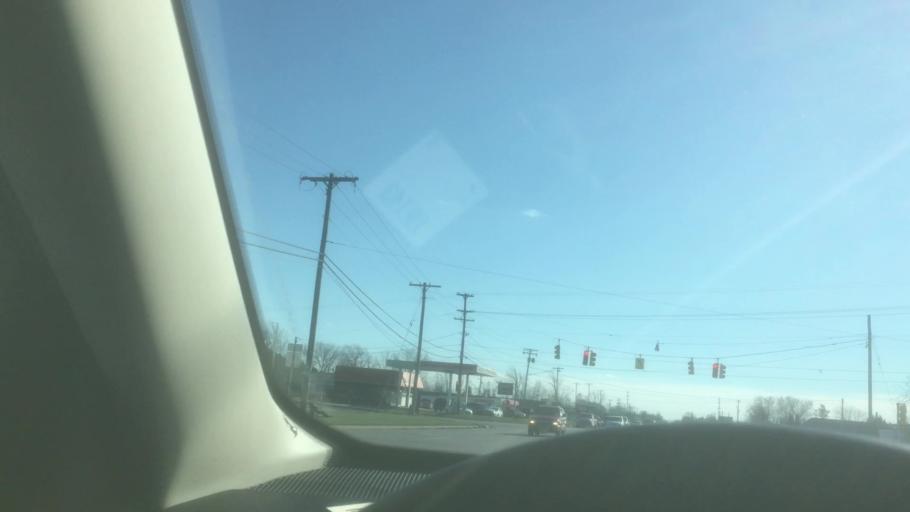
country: US
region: Michigan
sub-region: Bay County
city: Bay City
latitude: 43.5805
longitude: -83.8574
